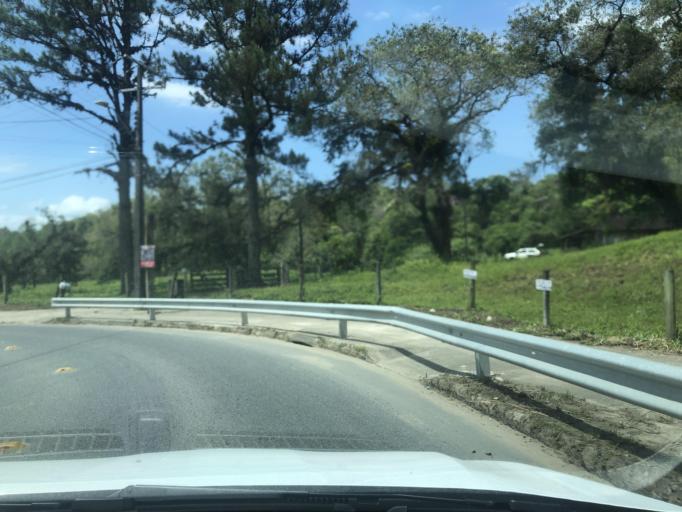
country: BR
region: Santa Catarina
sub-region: Joinville
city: Joinville
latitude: -26.3517
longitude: -48.7869
